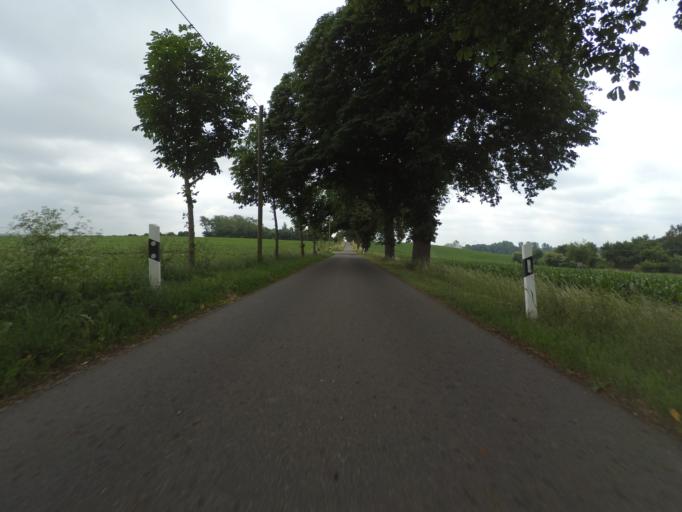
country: DE
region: Mecklenburg-Vorpommern
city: Krakow am See
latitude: 53.6364
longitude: 12.3413
